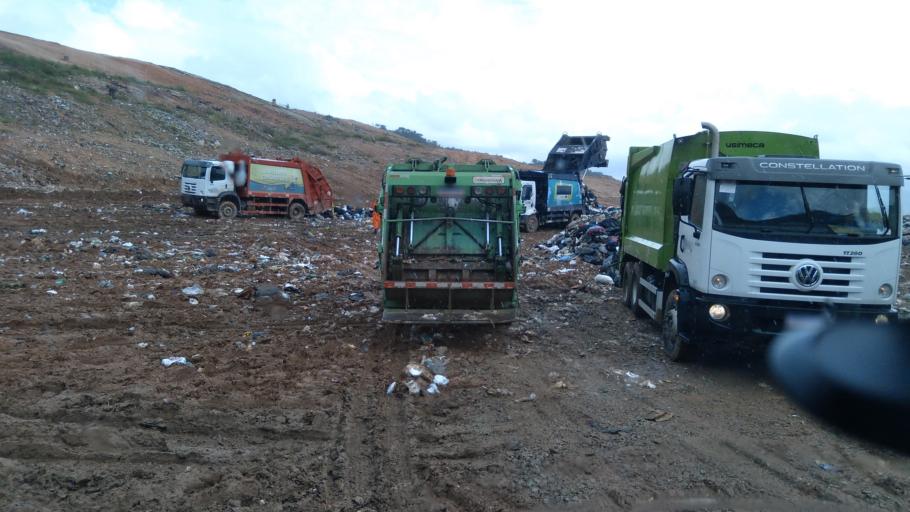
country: BR
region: Minas Gerais
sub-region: Santa Luzia
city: Santa Luzia
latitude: -19.8524
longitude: -43.8469
